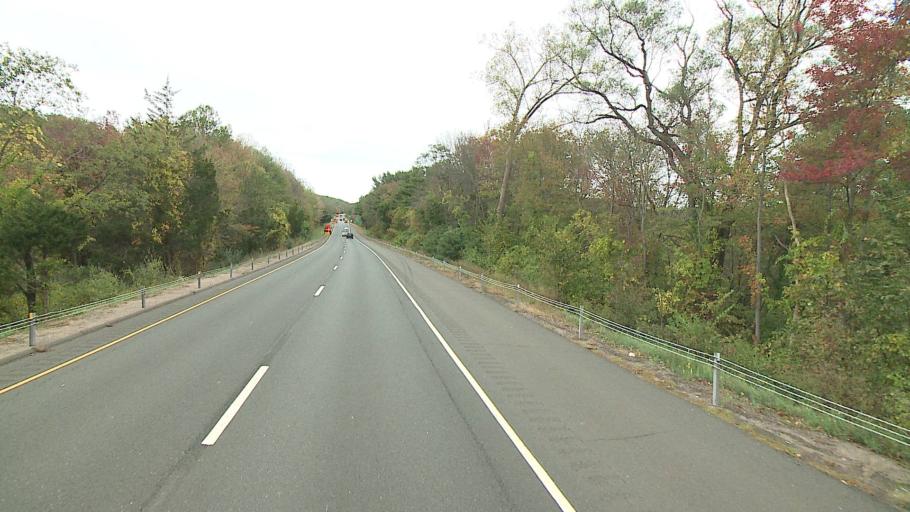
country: US
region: Connecticut
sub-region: Middlesex County
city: Higganum
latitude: 41.5035
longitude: -72.5813
